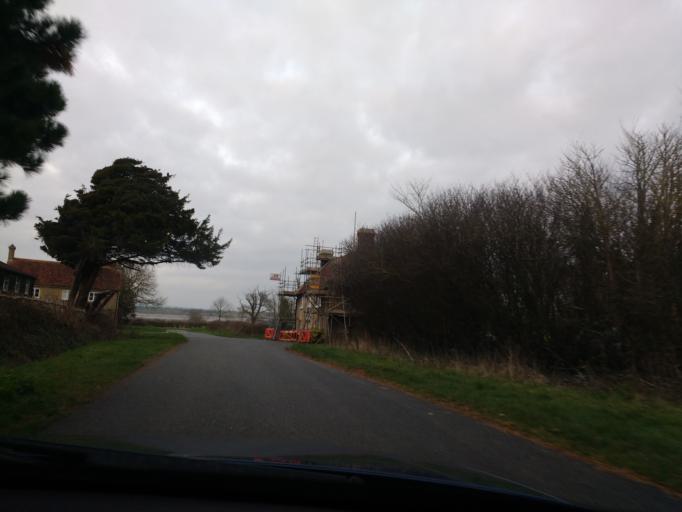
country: GB
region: England
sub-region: Isle of Wight
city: Shalfleet
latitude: 50.7134
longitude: -1.4011
